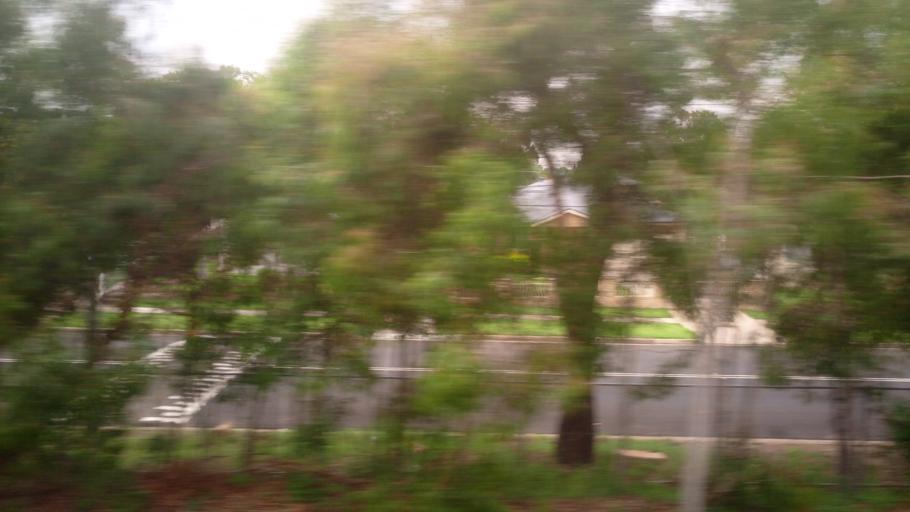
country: AU
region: New South Wales
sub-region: Parramatta
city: Constitution Hill
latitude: -33.8079
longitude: 150.9846
